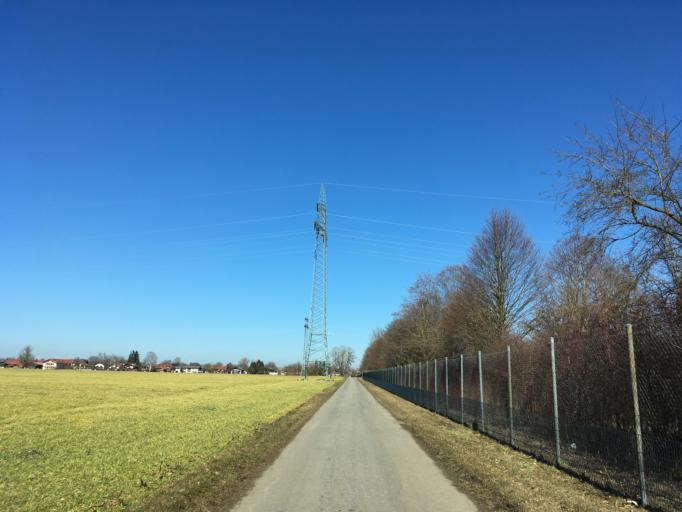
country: DE
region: Bavaria
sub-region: Upper Bavaria
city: Bad Aibling
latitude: 47.8468
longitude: 11.9881
